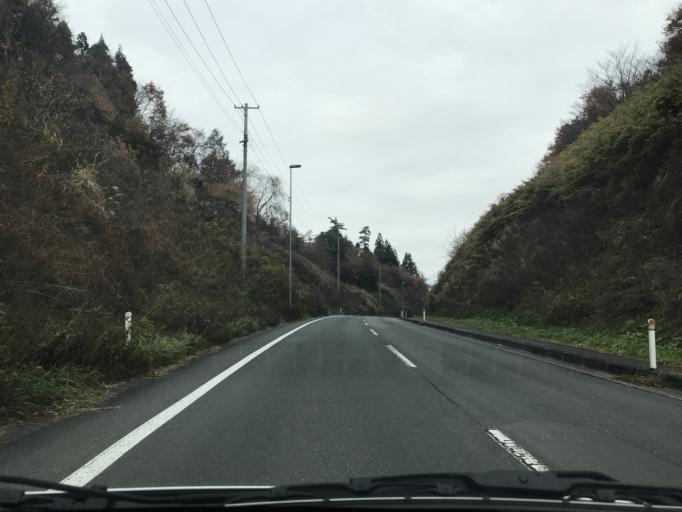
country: JP
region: Iwate
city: Mizusawa
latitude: 39.1653
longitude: 141.2044
